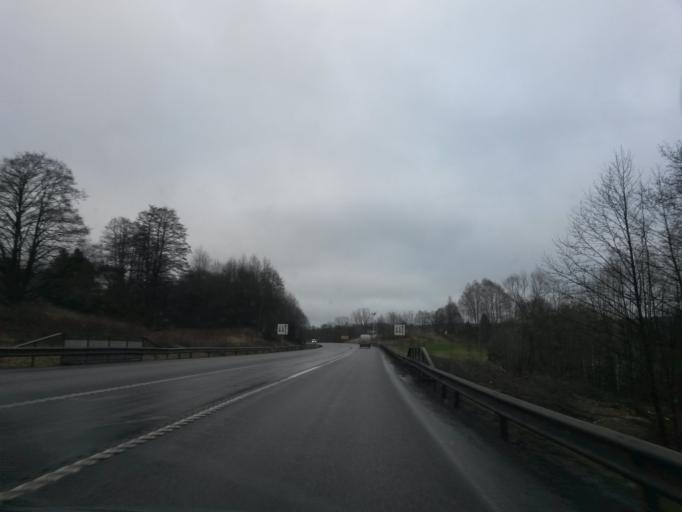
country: SE
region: Vaestra Goetaland
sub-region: Marks Kommun
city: Kinna
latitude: 57.5078
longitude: 12.7064
